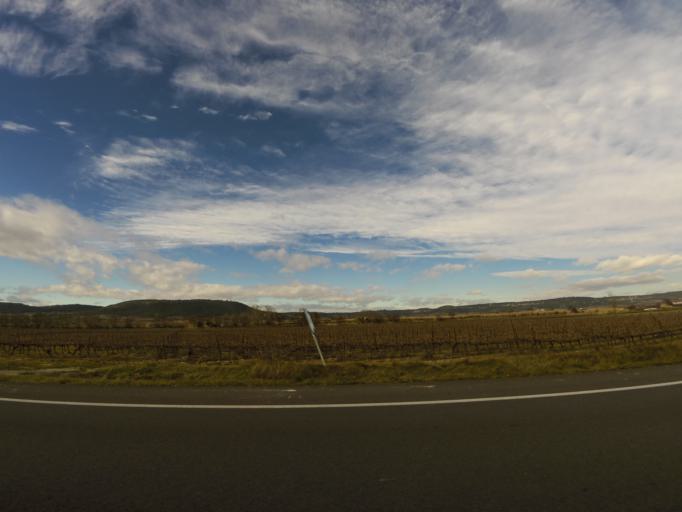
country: FR
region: Languedoc-Roussillon
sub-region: Departement du Gard
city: Nages-et-Solorgues
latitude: 43.7986
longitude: 4.2129
